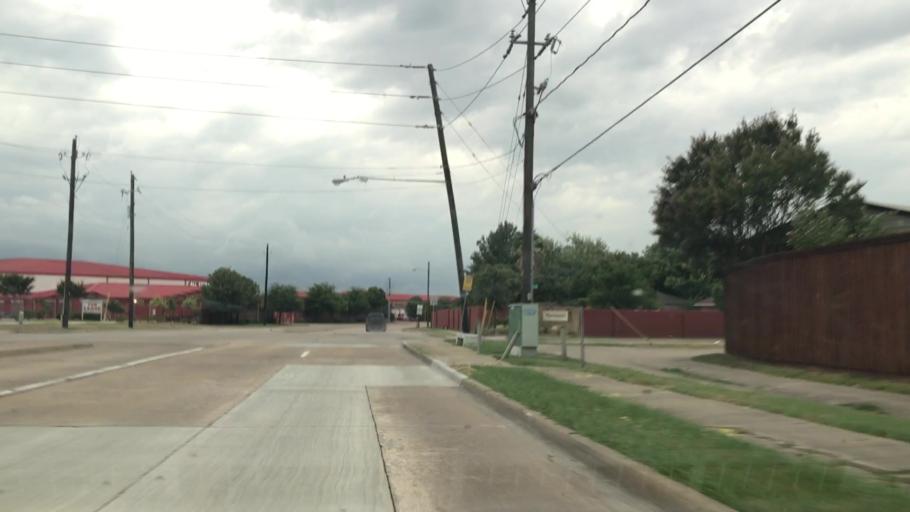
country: US
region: Texas
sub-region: Dallas County
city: Carrollton
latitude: 32.9901
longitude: -96.8673
